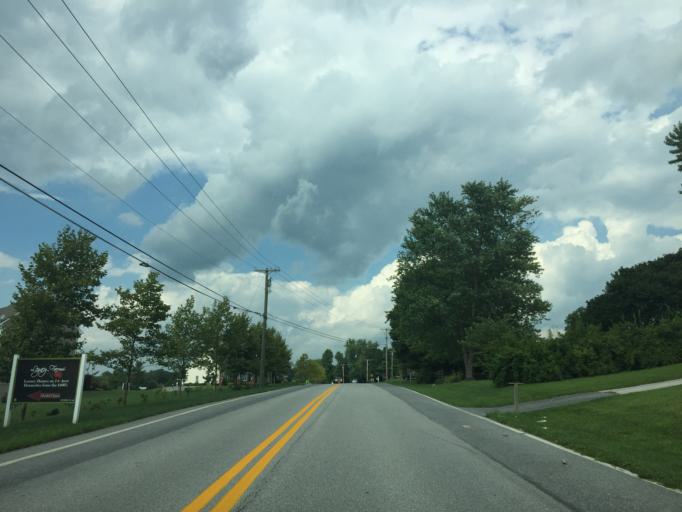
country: US
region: Maryland
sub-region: Carroll County
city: Westminster
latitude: 39.6020
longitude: -76.9745
